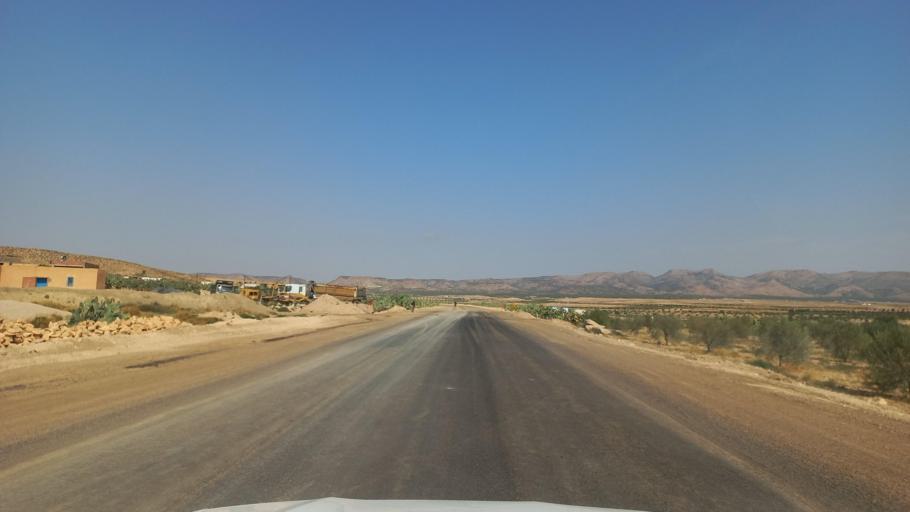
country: TN
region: Al Qasrayn
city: Sbiba
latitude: 35.3811
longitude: 9.0296
